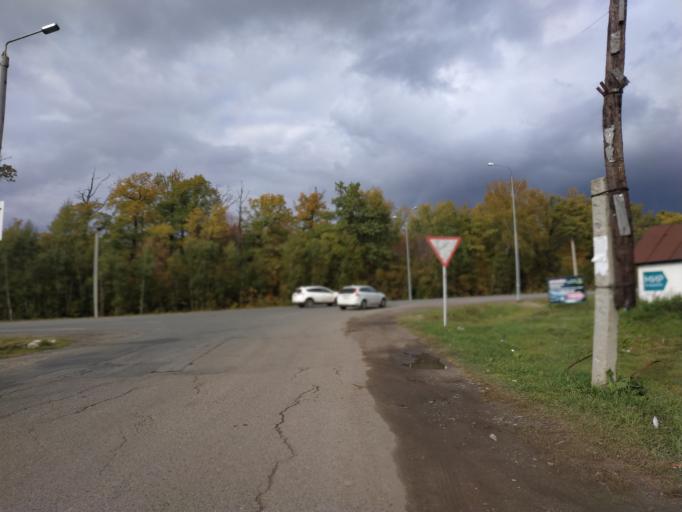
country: RU
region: Chuvashia
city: Ishley
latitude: 56.1335
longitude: 47.0867
